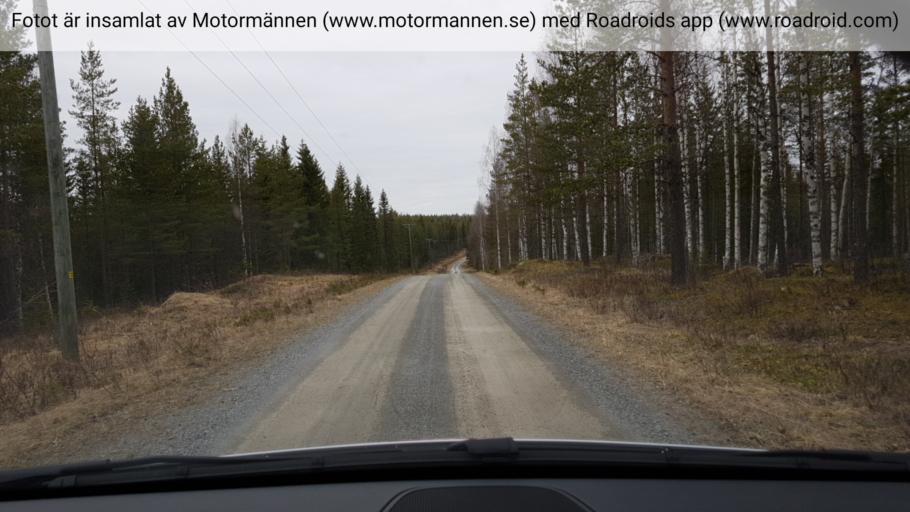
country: SE
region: Jaemtland
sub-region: Bergs Kommun
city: Hoverberg
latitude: 62.8420
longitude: 14.6196
